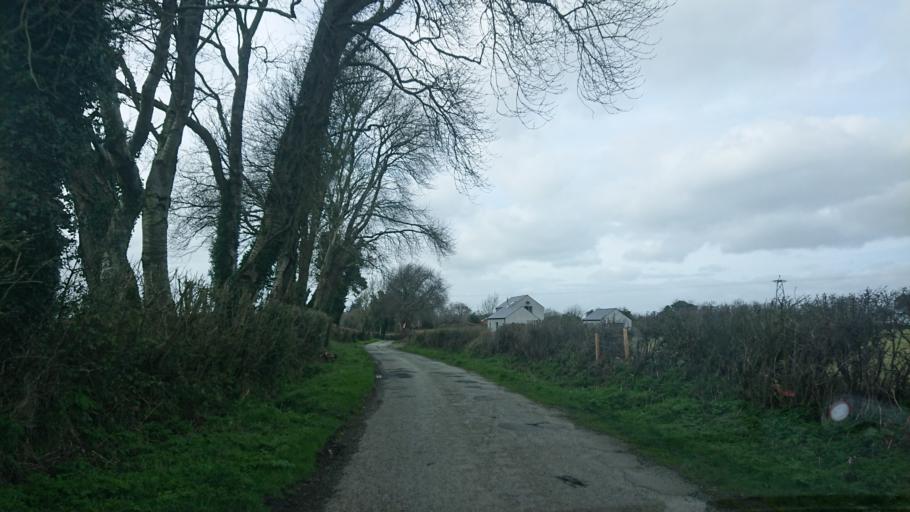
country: IE
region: Leinster
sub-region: Kildare
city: Eadestown
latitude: 53.1706
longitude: -6.6193
